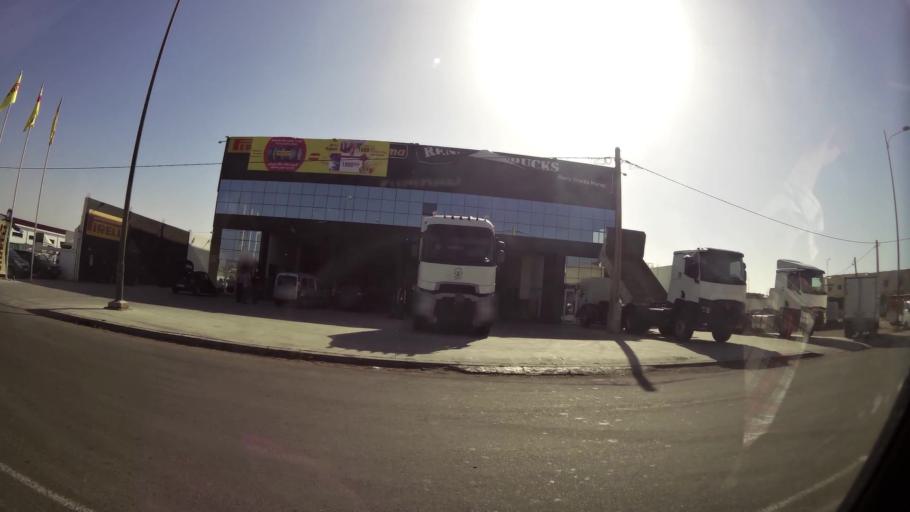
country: MA
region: Souss-Massa-Draa
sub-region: Inezgane-Ait Mellou
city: Inezgane
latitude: 30.3825
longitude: -9.5189
